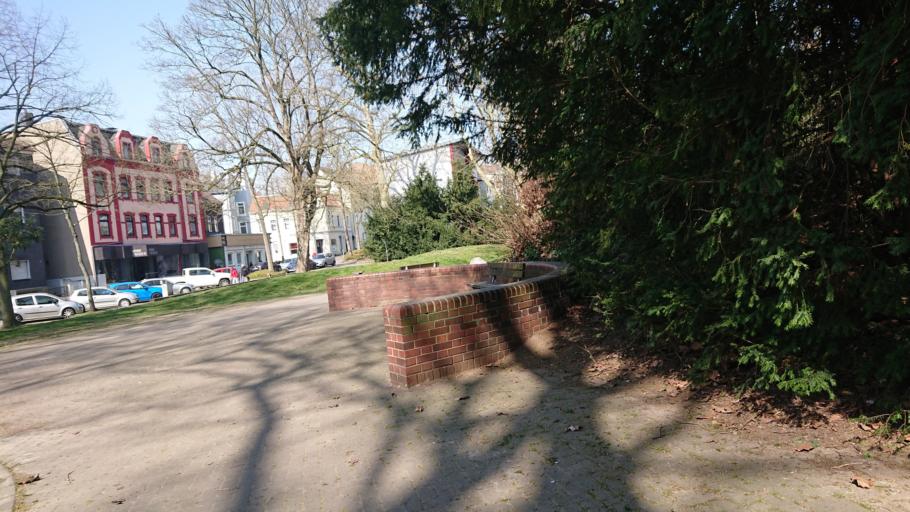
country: DE
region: North Rhine-Westphalia
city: Witten
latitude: 51.4885
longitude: 7.3072
